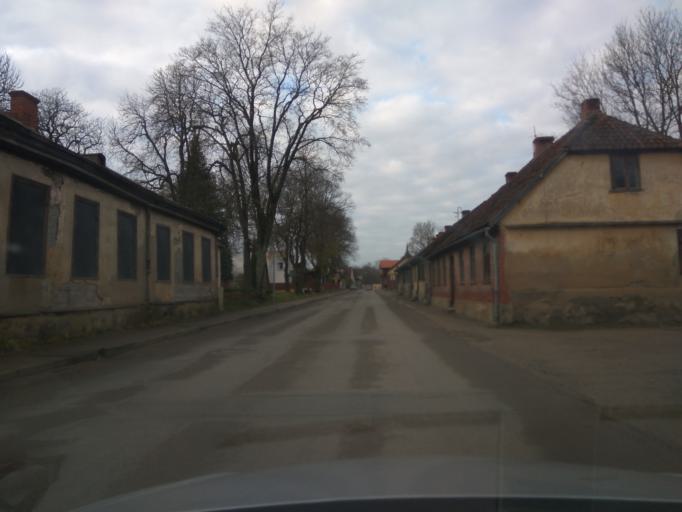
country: LV
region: Kuldigas Rajons
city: Kuldiga
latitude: 56.9642
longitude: 21.9773
